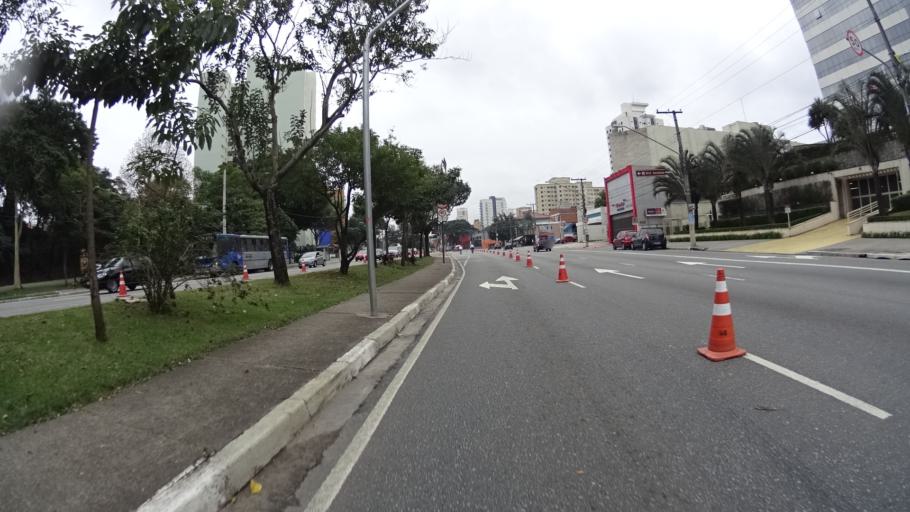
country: BR
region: Sao Paulo
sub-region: Sao Paulo
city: Sao Paulo
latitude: -23.4983
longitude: -46.6130
